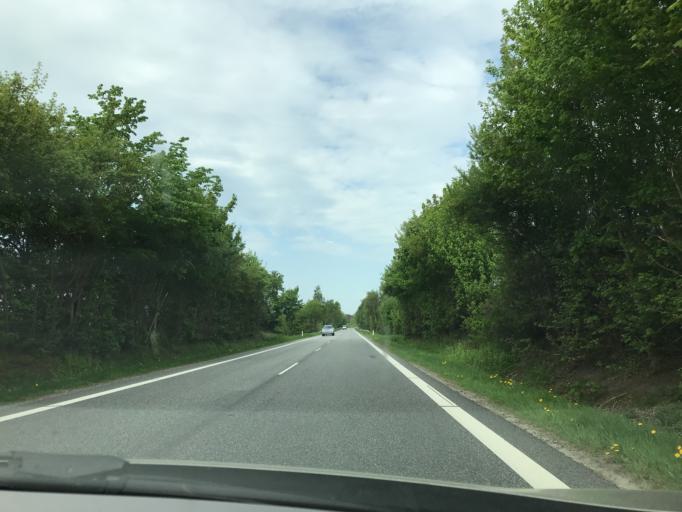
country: DK
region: South Denmark
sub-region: Assens Kommune
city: Assens
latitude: 55.3179
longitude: 9.9389
